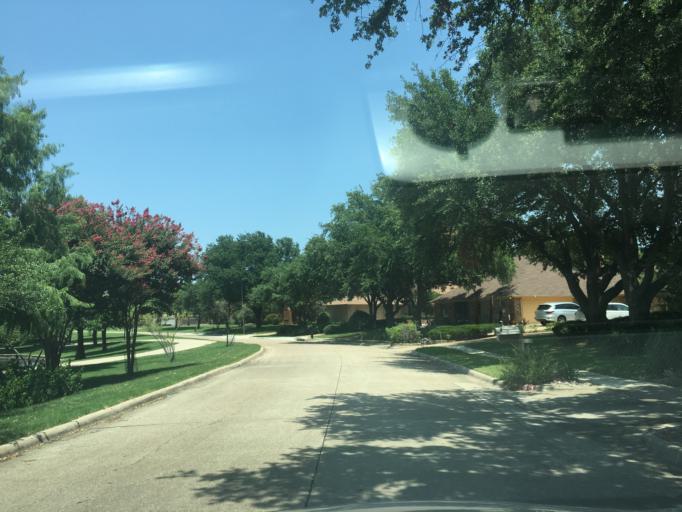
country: US
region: Texas
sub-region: Dallas County
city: Carrollton
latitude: 32.9458
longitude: -96.8611
